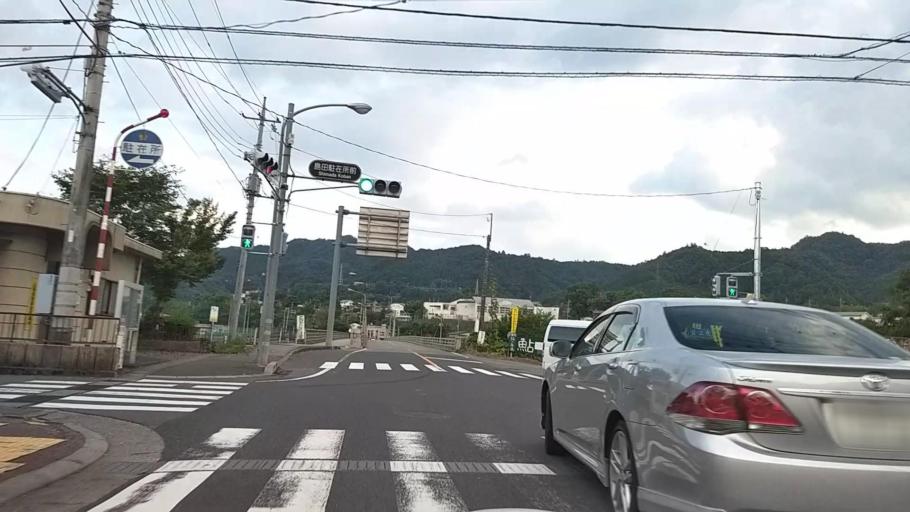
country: JP
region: Yamanashi
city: Uenohara
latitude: 35.6180
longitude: 139.1184
